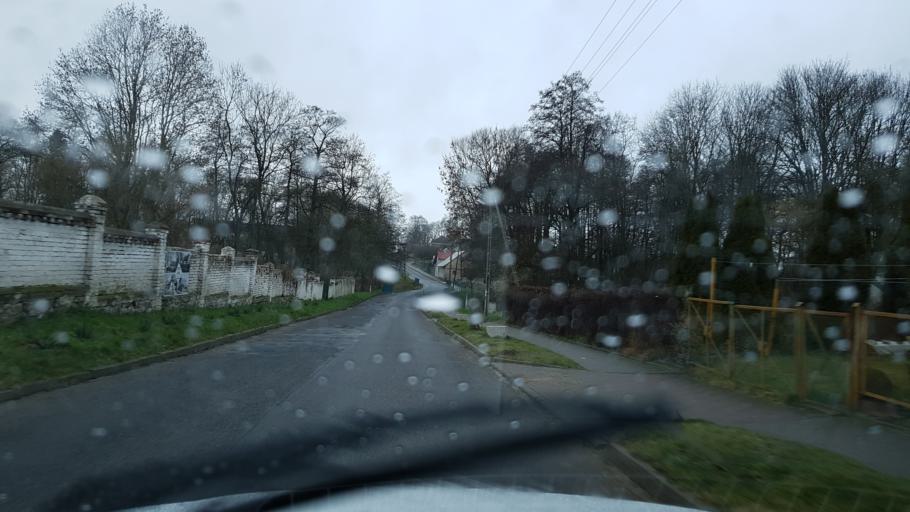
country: PL
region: West Pomeranian Voivodeship
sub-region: Powiat lobeski
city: Dobra
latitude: 53.5967
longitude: 15.3896
